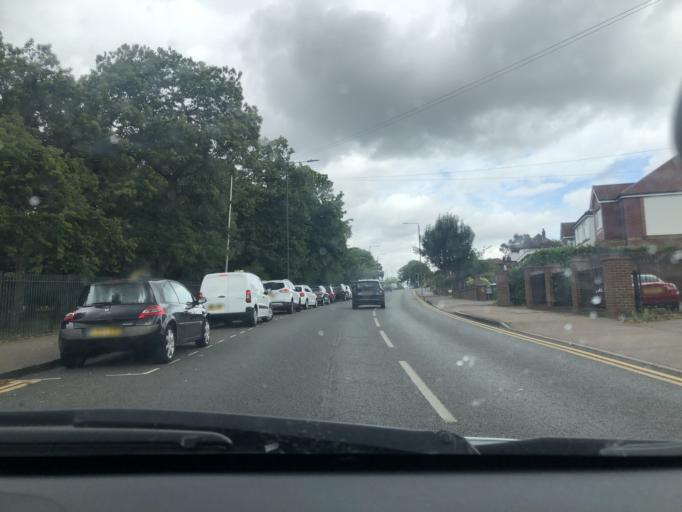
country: GB
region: England
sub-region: Greater London
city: Welling
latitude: 51.4544
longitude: 0.1227
